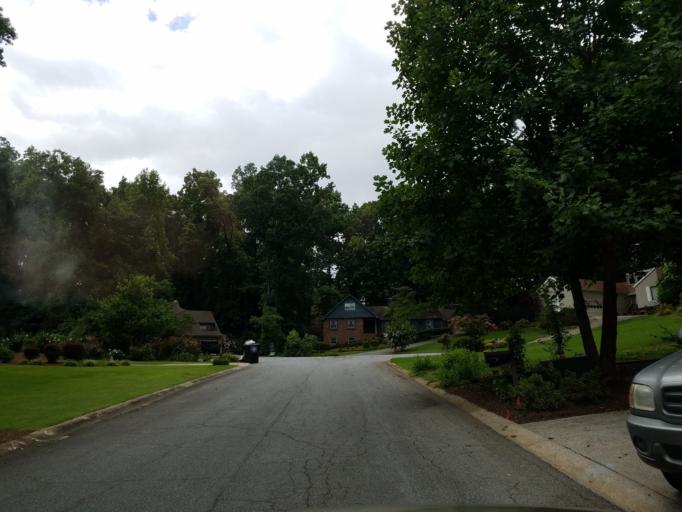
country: US
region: Georgia
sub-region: Cobb County
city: Marietta
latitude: 33.9580
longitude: -84.4866
